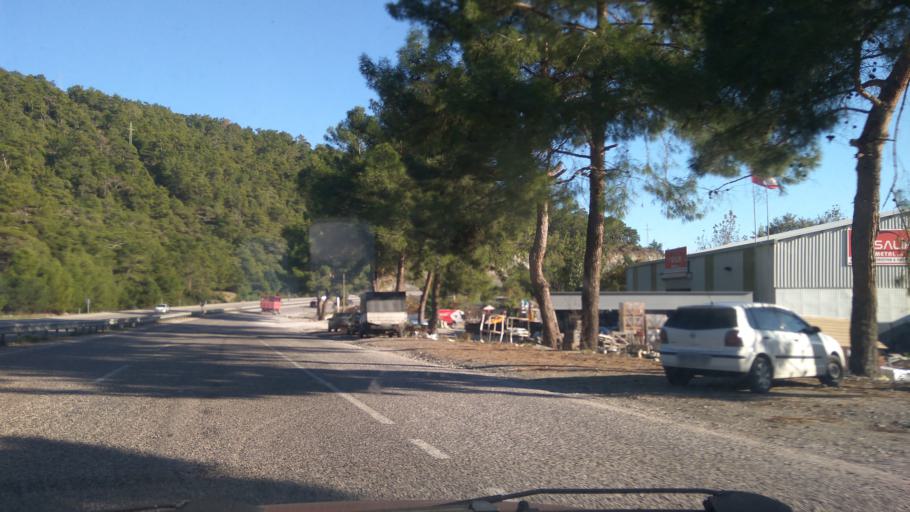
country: TR
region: Antalya
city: Kemer
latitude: 36.5821
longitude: 30.5516
